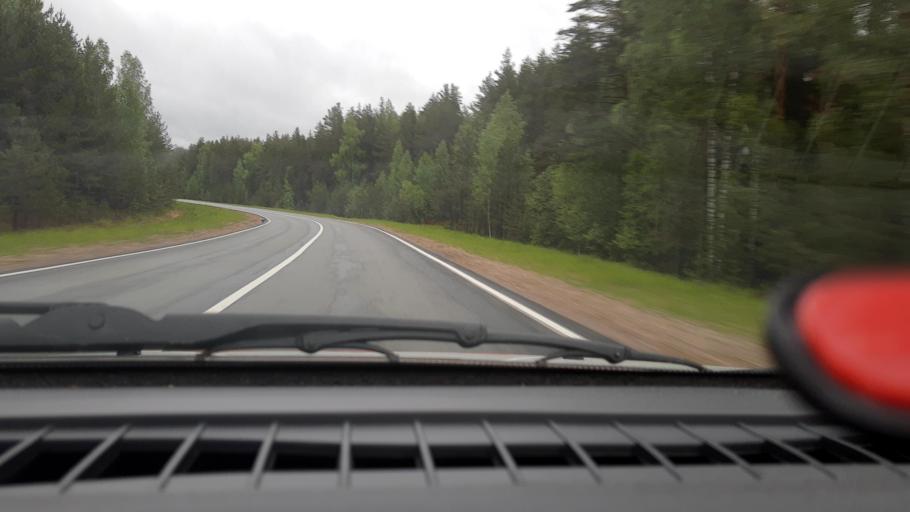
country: RU
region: Nizjnij Novgorod
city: Krasnyye Baki
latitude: 57.2028
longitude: 45.4587
